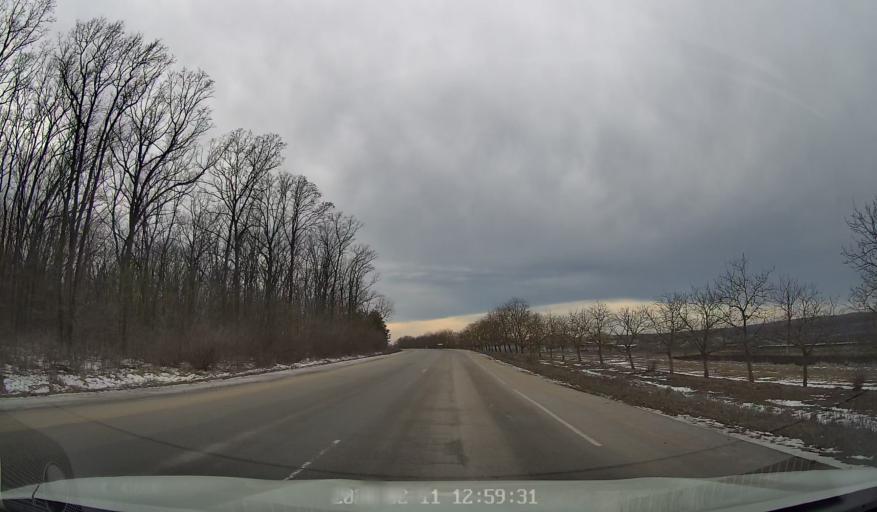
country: MD
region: Briceni
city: Briceni
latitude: 48.3285
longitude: 27.0329
